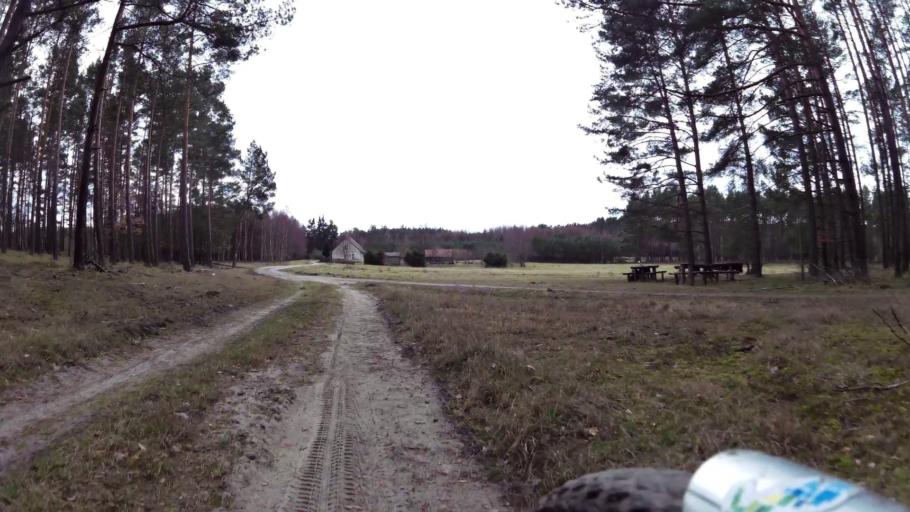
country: PL
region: Pomeranian Voivodeship
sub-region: Powiat bytowski
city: Kolczyglowy
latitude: 54.1561
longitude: 17.1870
